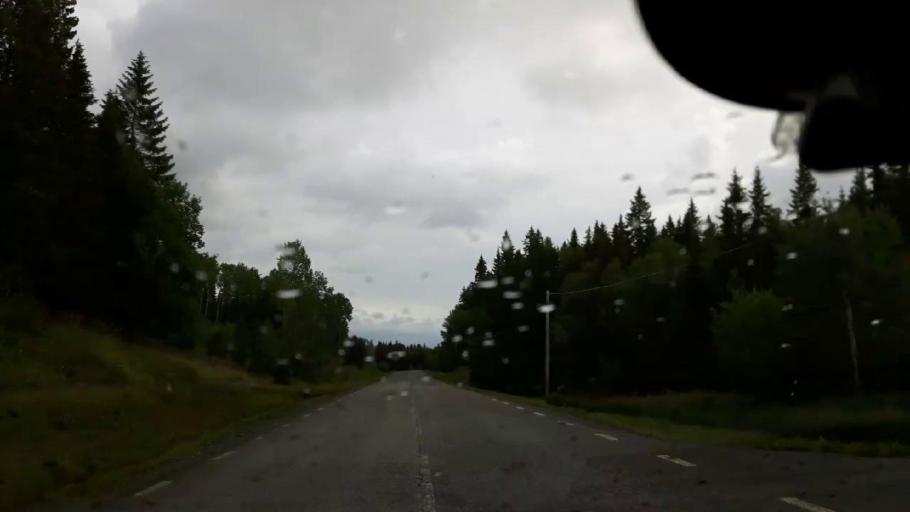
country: SE
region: Jaemtland
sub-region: Krokoms Kommun
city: Valla
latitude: 63.4163
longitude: 13.7959
